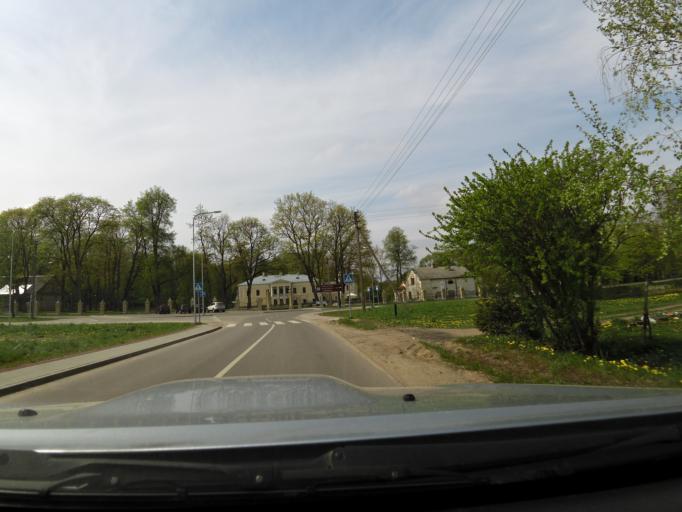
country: LT
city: Salcininkai
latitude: 54.4334
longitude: 25.3008
